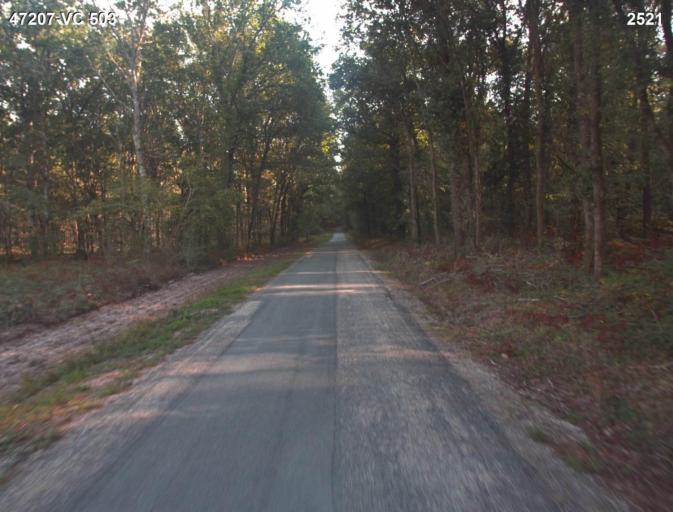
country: FR
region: Aquitaine
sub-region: Departement du Lot-et-Garonne
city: Barbaste
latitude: 44.1865
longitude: 0.2351
